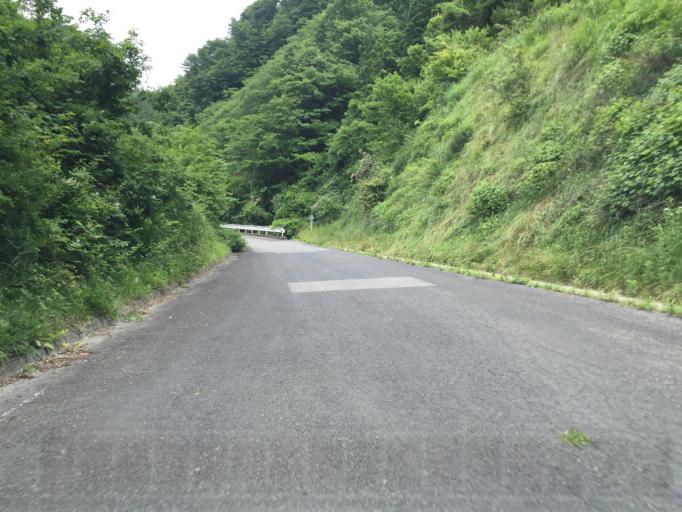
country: JP
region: Miyagi
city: Marumori
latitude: 37.7940
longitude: 140.7741
